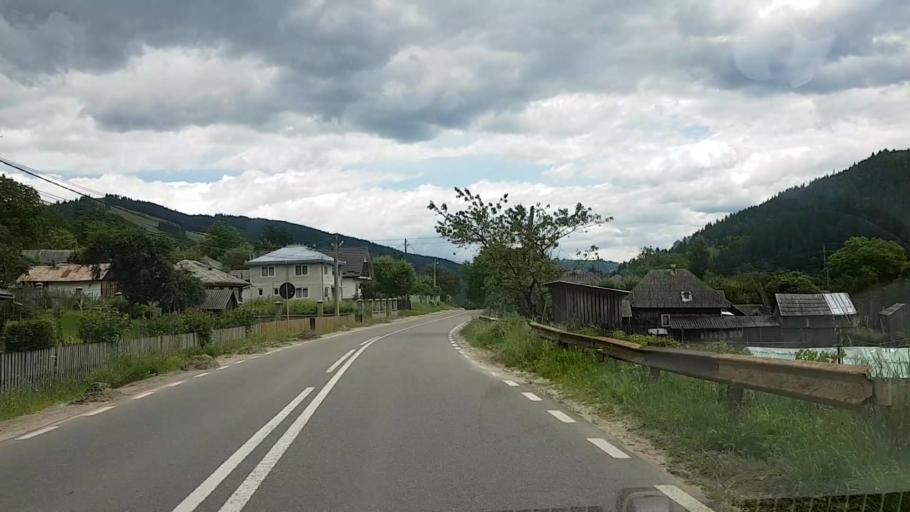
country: RO
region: Neamt
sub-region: Comuna Poiana Teiului
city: Poiana Teiului
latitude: 47.1186
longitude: 25.9164
